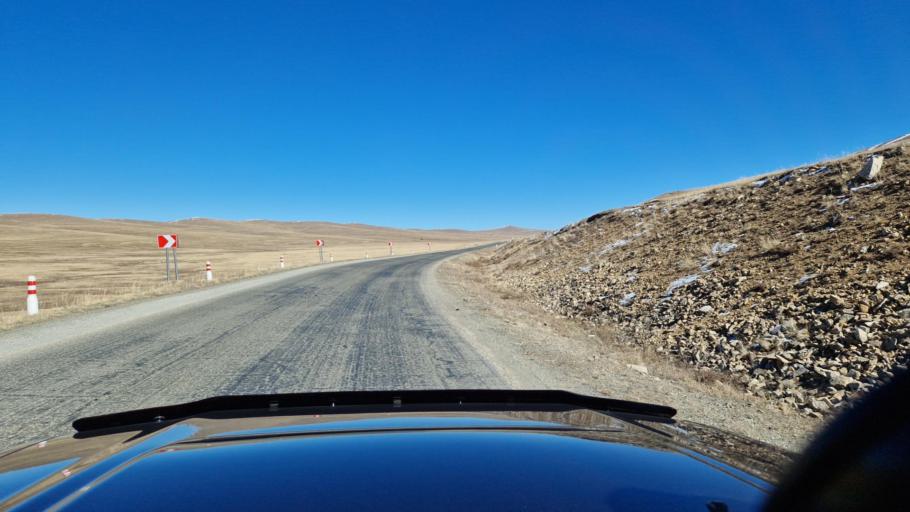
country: MN
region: Hentiy
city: Modot
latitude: 47.7849
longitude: 108.6673
